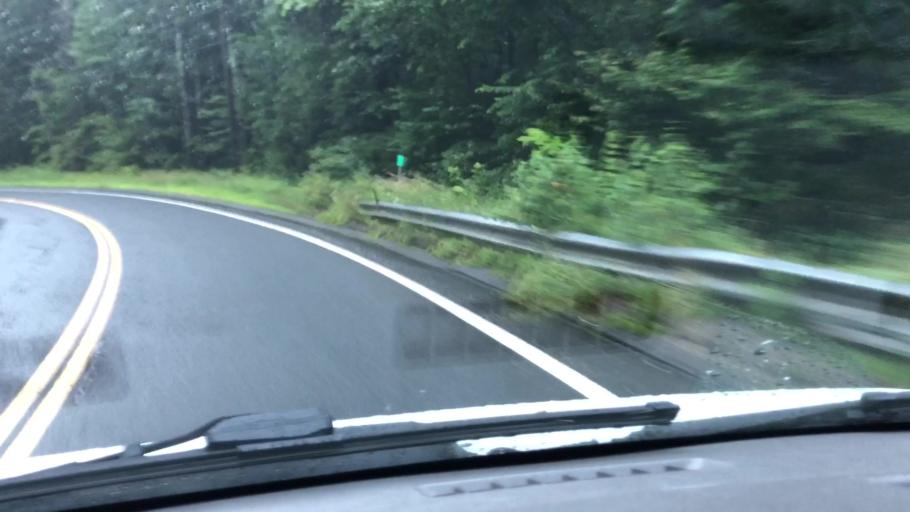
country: US
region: Massachusetts
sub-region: Hampshire County
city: Westhampton
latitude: 42.2841
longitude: -72.8547
